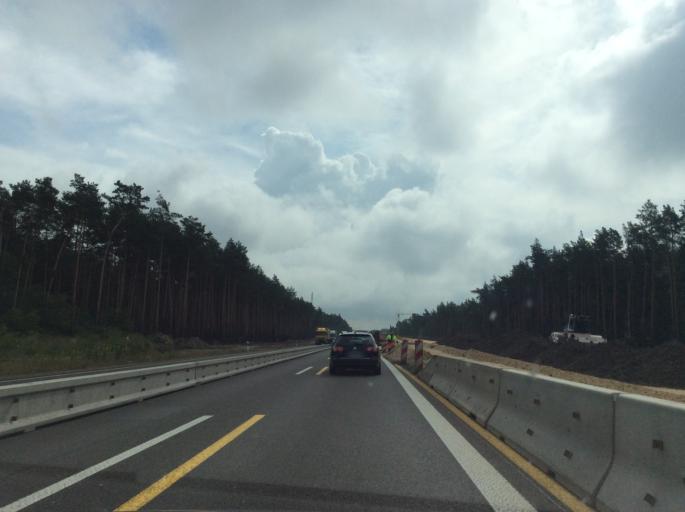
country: DE
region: Brandenburg
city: Storkow
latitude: 52.3124
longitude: 13.9358
